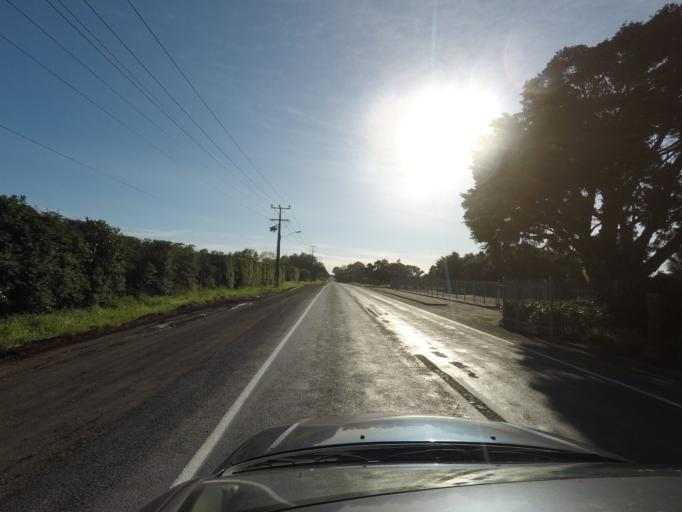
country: NZ
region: Auckland
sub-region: Auckland
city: Papakura
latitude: -37.0160
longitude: 174.9408
